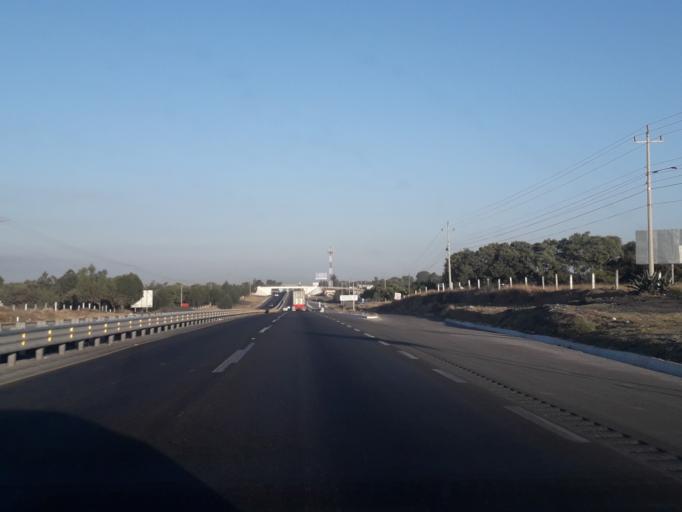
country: MX
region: Puebla
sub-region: Amozoc
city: Amozoc de Mota
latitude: 19.0558
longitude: -98.0579
